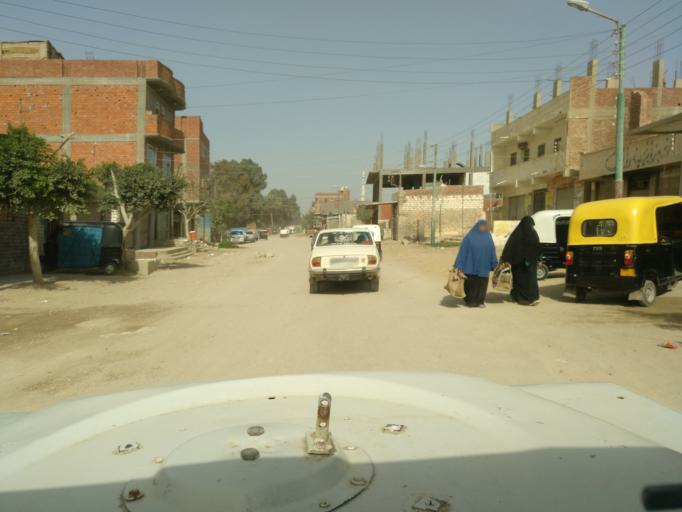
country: EG
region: Al Buhayrah
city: Beheira
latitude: 30.3706
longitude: 30.3557
